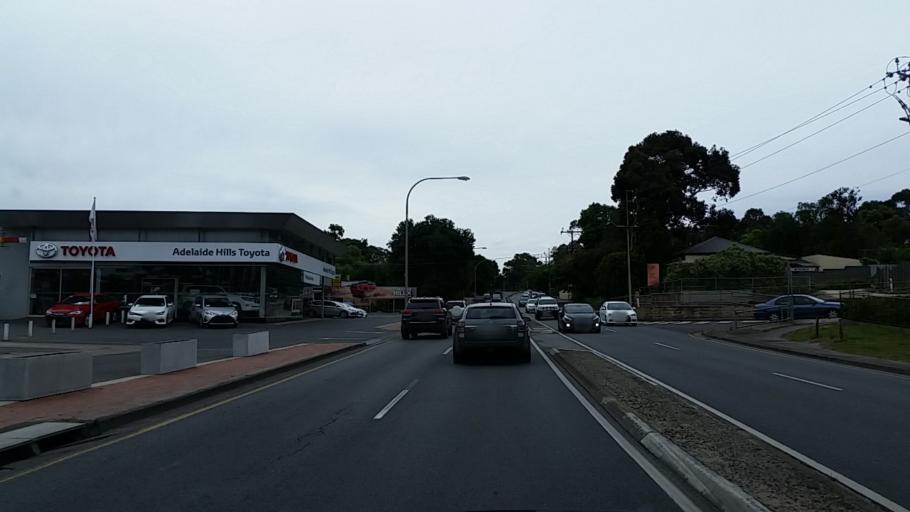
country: AU
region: South Australia
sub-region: Mount Barker
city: Mount Barker
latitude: -35.0639
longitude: 138.8542
